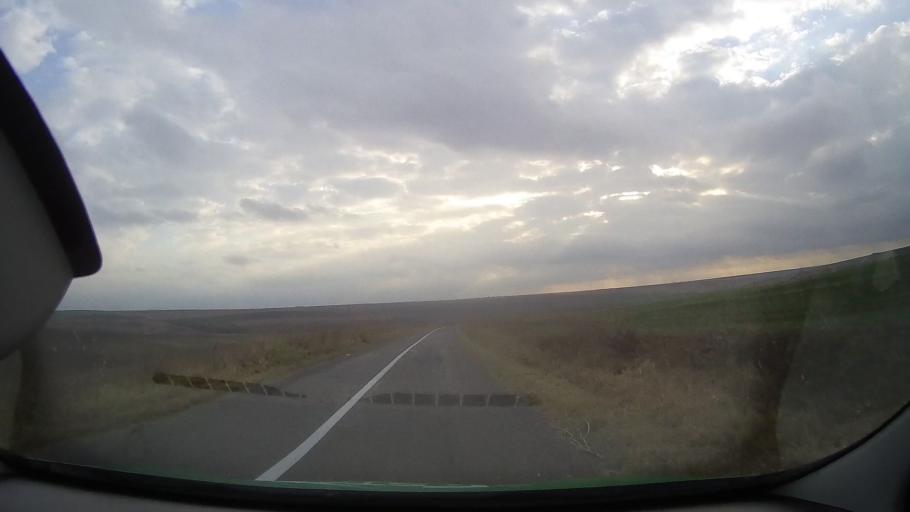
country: RO
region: Constanta
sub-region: Comuna Deleni
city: Pietreni
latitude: 44.1205
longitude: 28.1040
